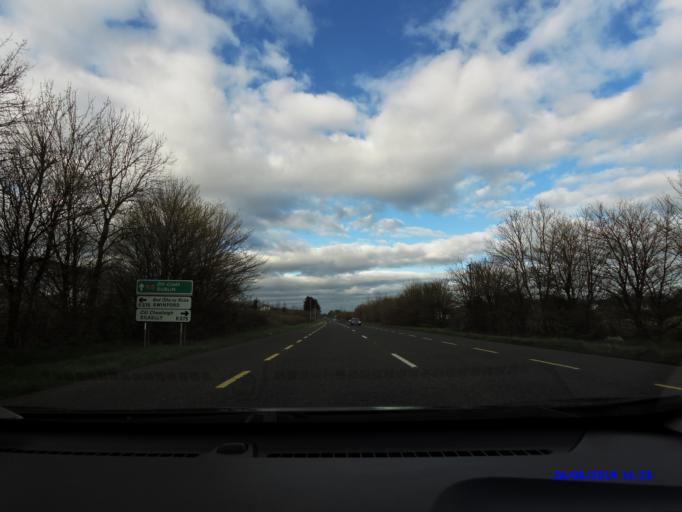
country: IE
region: Connaught
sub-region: Maigh Eo
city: Swinford
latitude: 53.9347
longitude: -8.9425
